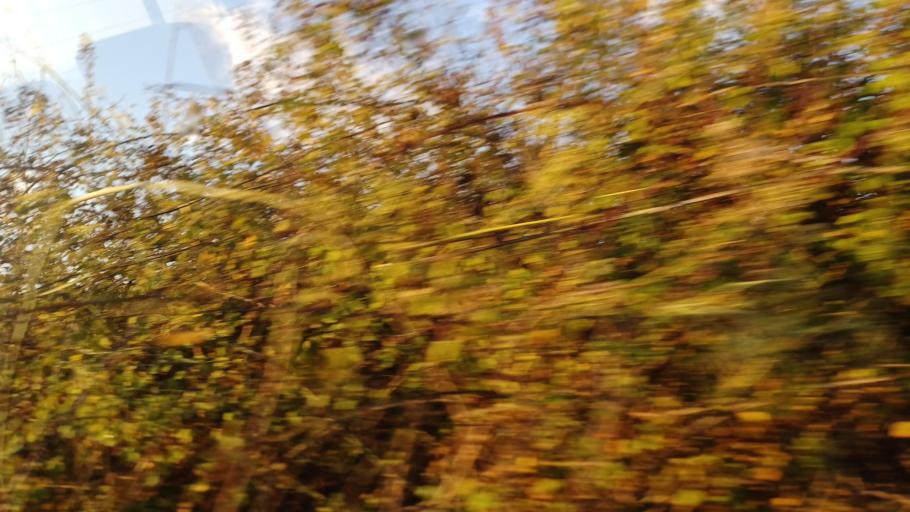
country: CY
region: Pafos
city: Tala
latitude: 34.8990
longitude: 32.4998
